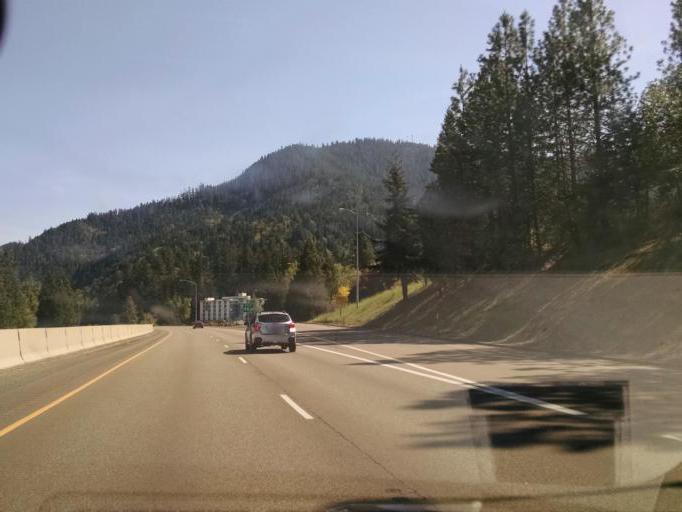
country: US
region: Oregon
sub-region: Douglas County
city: Canyonville
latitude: 42.9304
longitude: -123.2829
